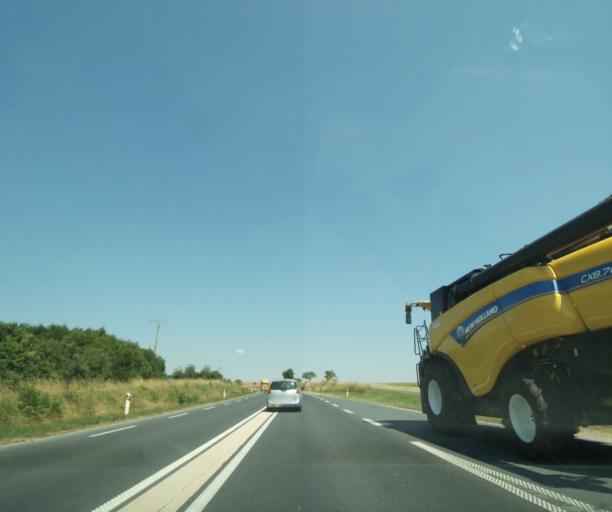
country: FR
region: Champagne-Ardenne
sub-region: Departement de la Marne
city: Mourmelon-le-Grand
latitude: 49.0667
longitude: 4.2966
